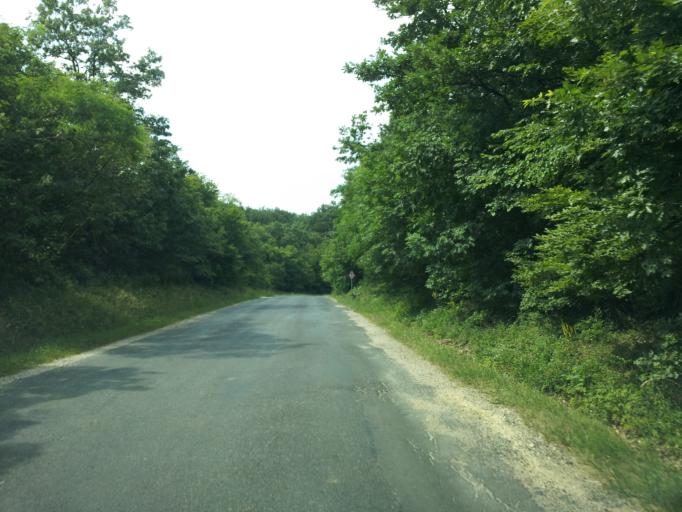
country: HU
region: Veszprem
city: Zanka
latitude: 46.9347
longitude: 17.7013
